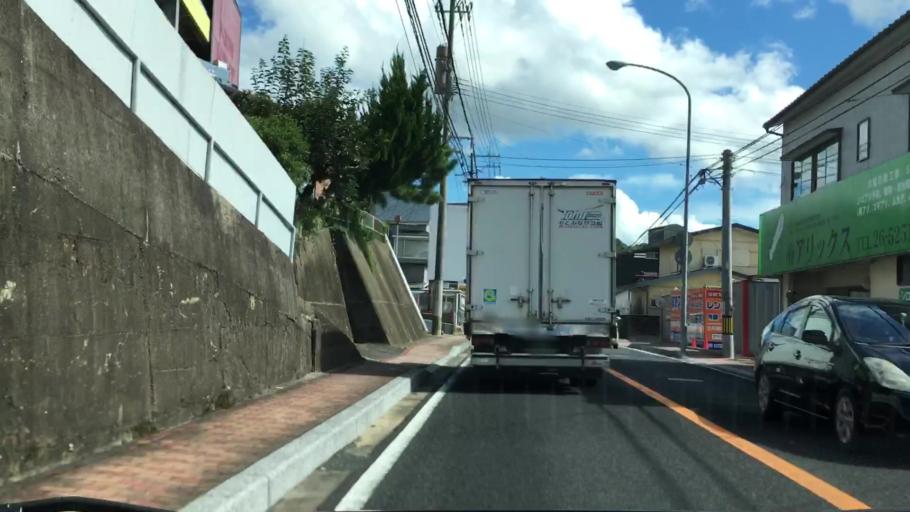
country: JP
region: Nagasaki
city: Sasebo
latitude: 33.1425
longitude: 129.7866
